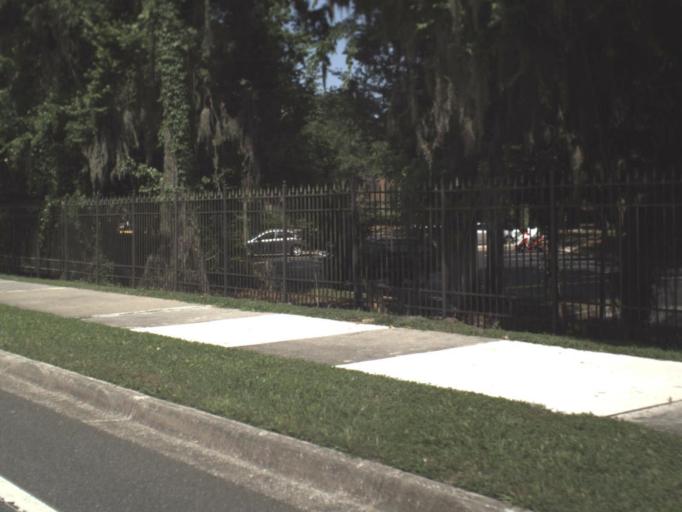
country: US
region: Florida
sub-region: Alachua County
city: Gainesville
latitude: 29.6101
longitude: -82.3622
